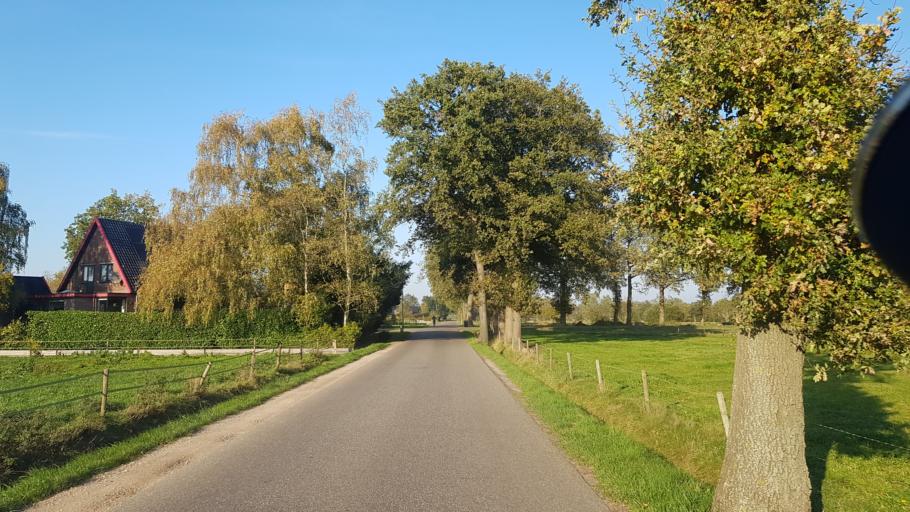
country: NL
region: Gelderland
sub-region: Gemeente Apeldoorn
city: Loenen
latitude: 52.1813
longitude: 6.0294
